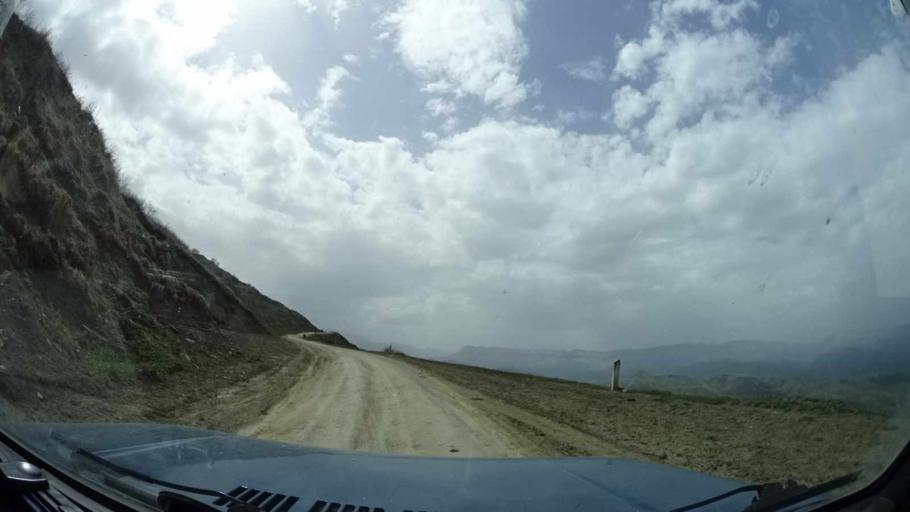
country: RU
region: Dagestan
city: Kubachi
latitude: 42.0894
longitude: 47.5854
